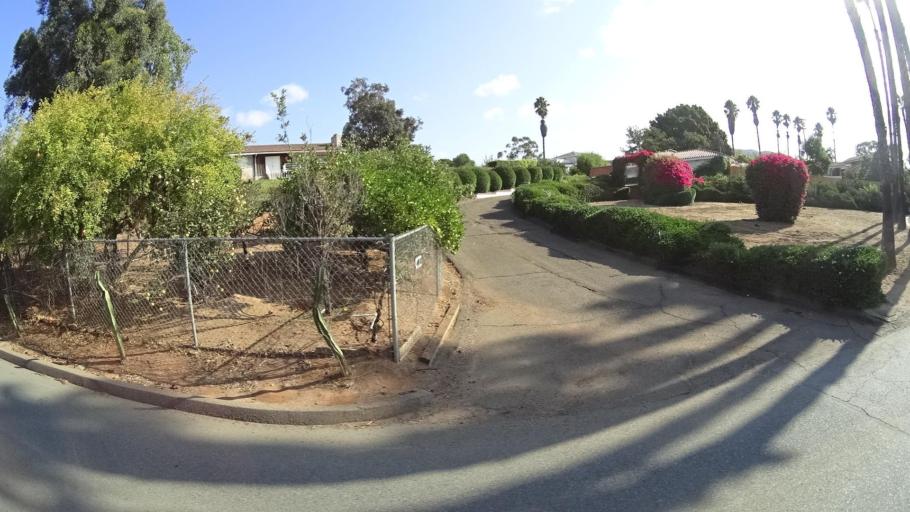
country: US
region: California
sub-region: San Diego County
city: Eucalyptus Hills
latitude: 32.8852
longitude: -116.9397
